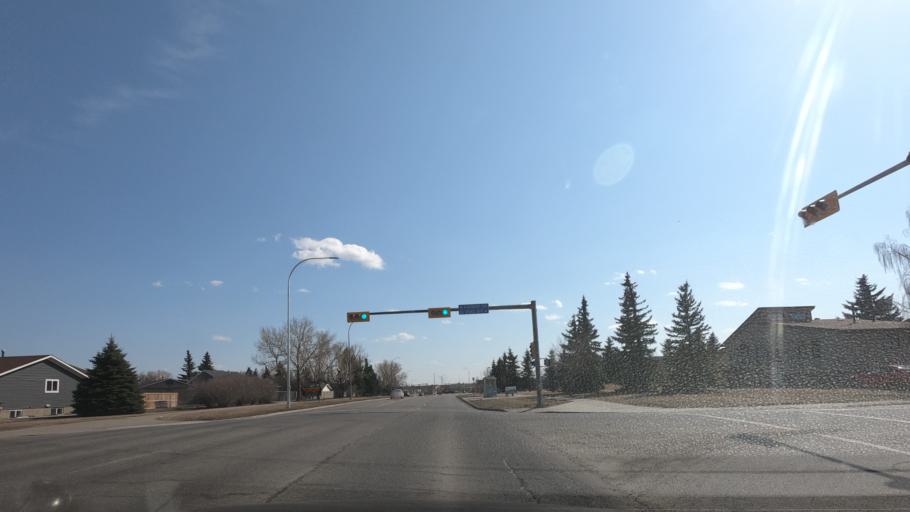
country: CA
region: Alberta
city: Airdrie
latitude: 51.2733
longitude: -113.9899
